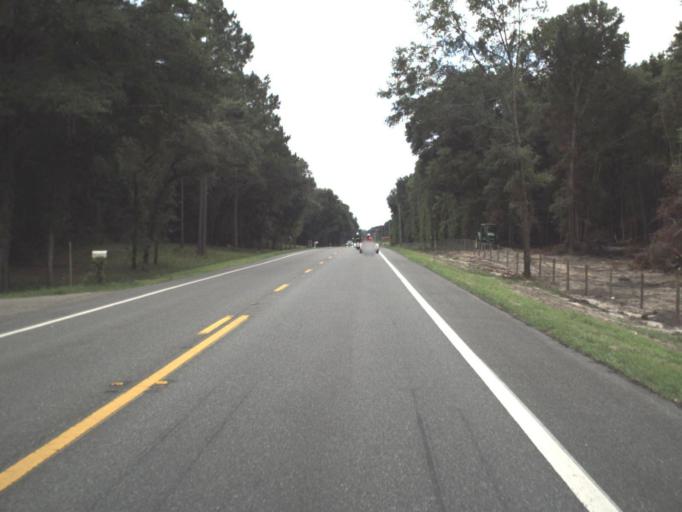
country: US
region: Florida
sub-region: Alachua County
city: Archer
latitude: 29.5631
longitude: -82.5373
